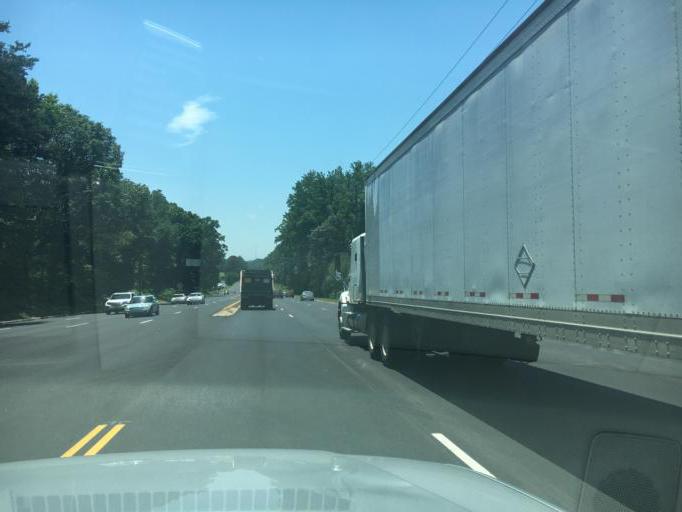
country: US
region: South Carolina
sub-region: Greenville County
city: Travelers Rest
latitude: 34.9363
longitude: -82.4471
